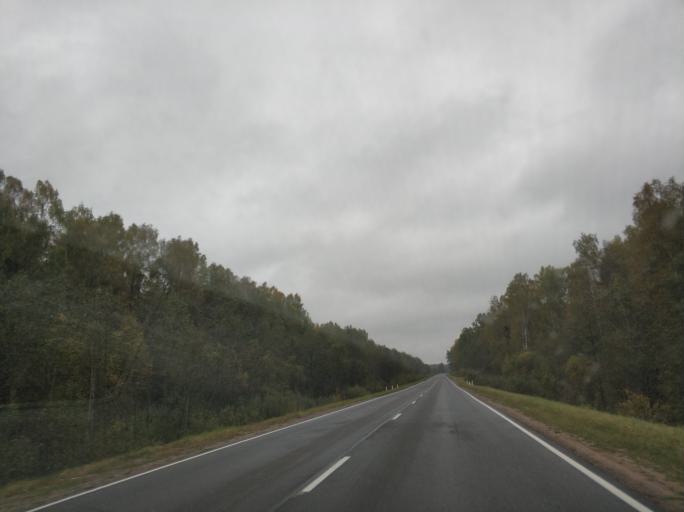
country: BY
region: Vitebsk
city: Rasony
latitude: 56.0897
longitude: 28.7200
